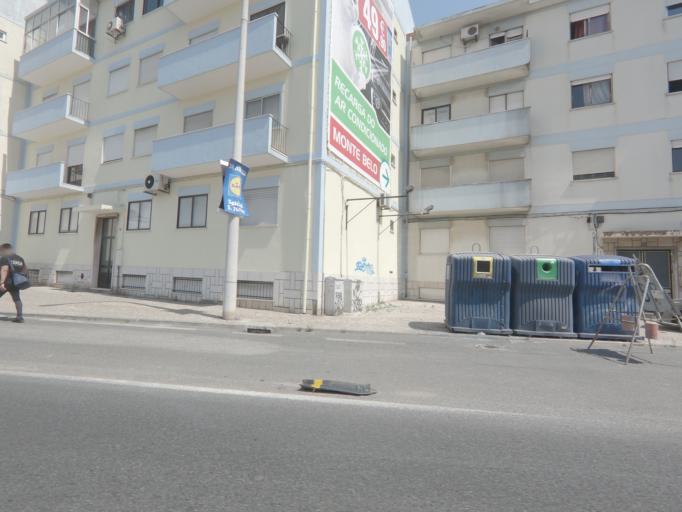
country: PT
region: Setubal
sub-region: Setubal
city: Setubal
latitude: 38.5336
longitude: -8.8841
